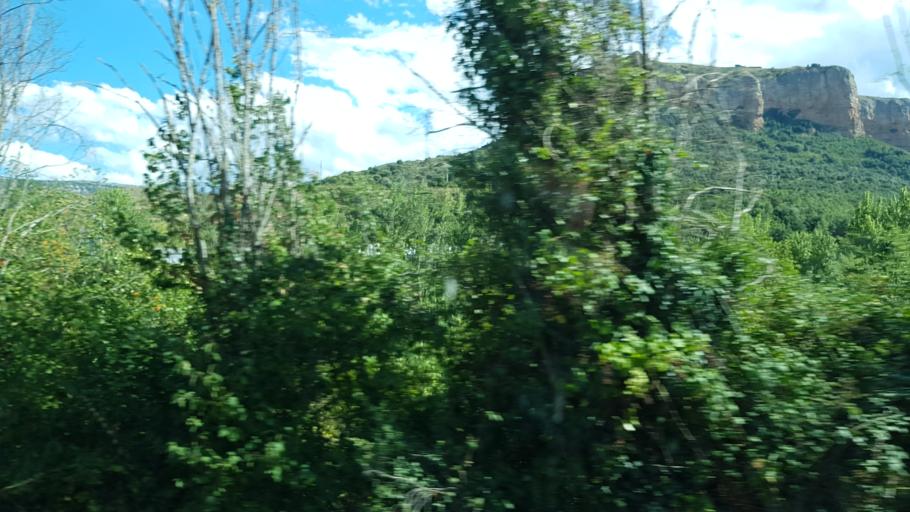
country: ES
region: La Rioja
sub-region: Provincia de La Rioja
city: Viguera
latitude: 42.3110
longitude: -2.5529
